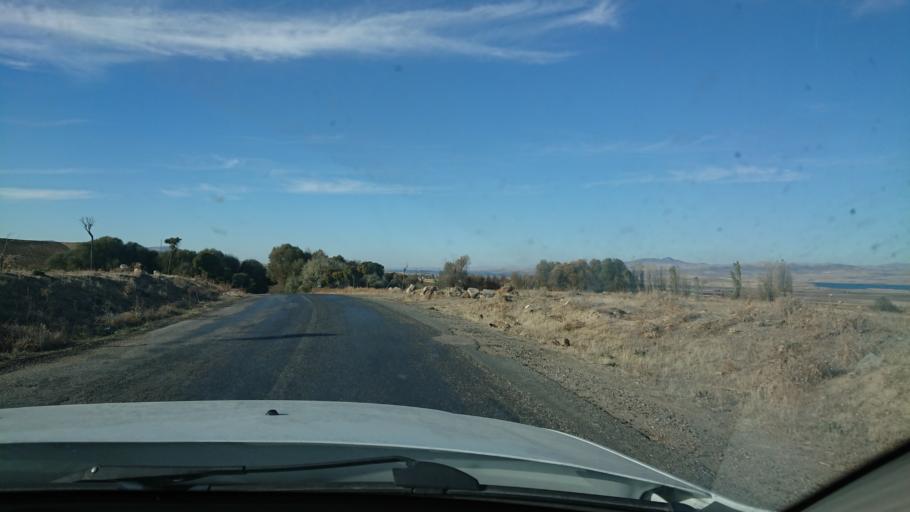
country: TR
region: Aksaray
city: Sariyahsi
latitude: 38.9692
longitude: 33.8683
